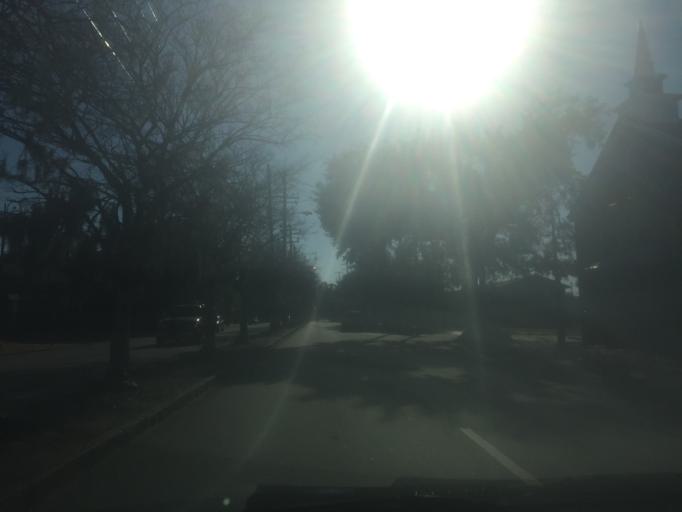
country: US
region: Georgia
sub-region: Chatham County
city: Savannah
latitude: 32.0682
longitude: -81.1019
